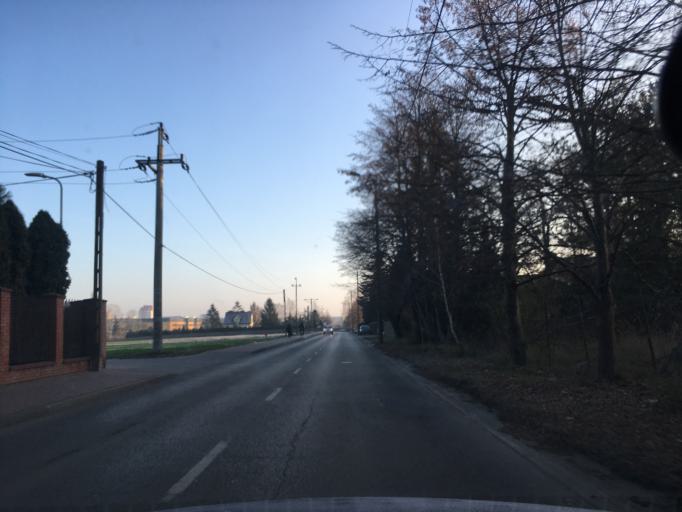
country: PL
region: Masovian Voivodeship
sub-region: Powiat piaseczynski
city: Piaseczno
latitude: 52.0709
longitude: 21.0057
